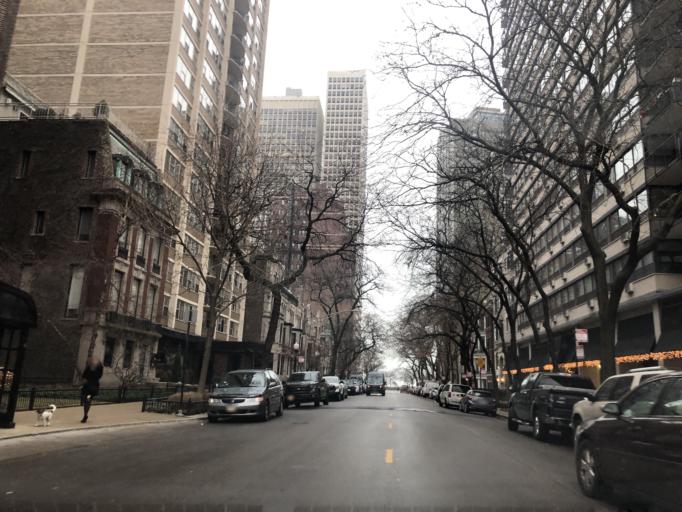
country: US
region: Illinois
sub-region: Cook County
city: Chicago
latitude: 41.9024
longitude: -87.6275
